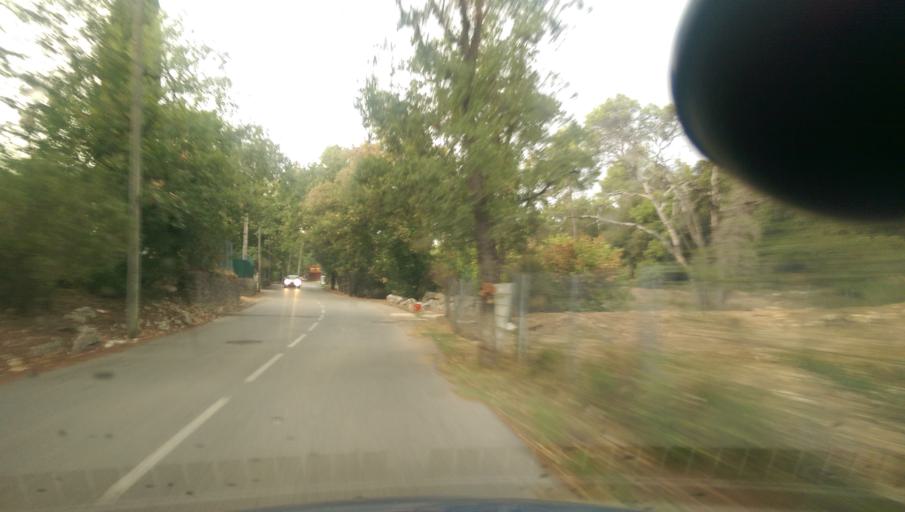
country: FR
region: Provence-Alpes-Cote d'Azur
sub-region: Departement des Alpes-Maritimes
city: Valbonne
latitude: 43.6403
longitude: 7.0379
